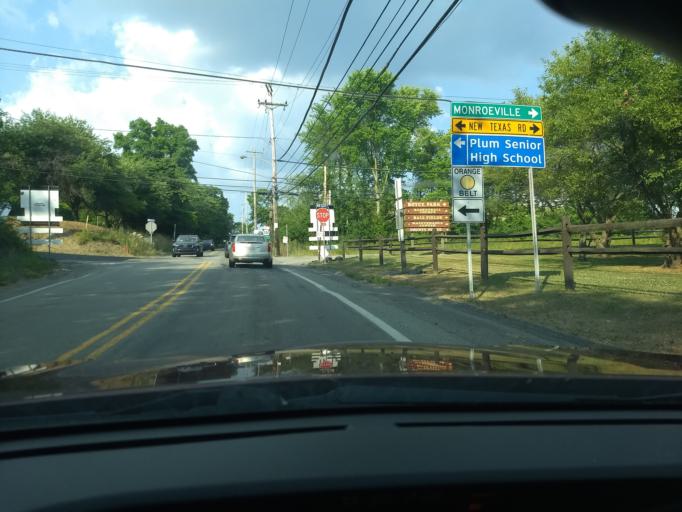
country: US
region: Pennsylvania
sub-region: Allegheny County
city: Plum
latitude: 40.4777
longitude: -79.7364
